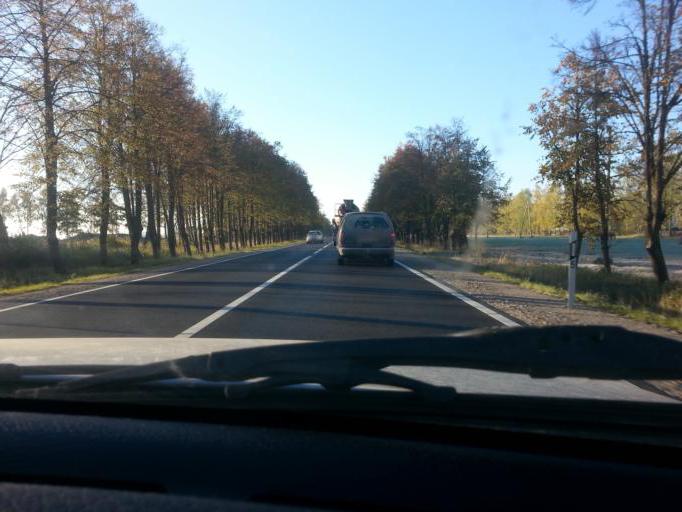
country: LV
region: Jelgava
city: Jelgava
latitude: 56.5049
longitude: 23.7007
